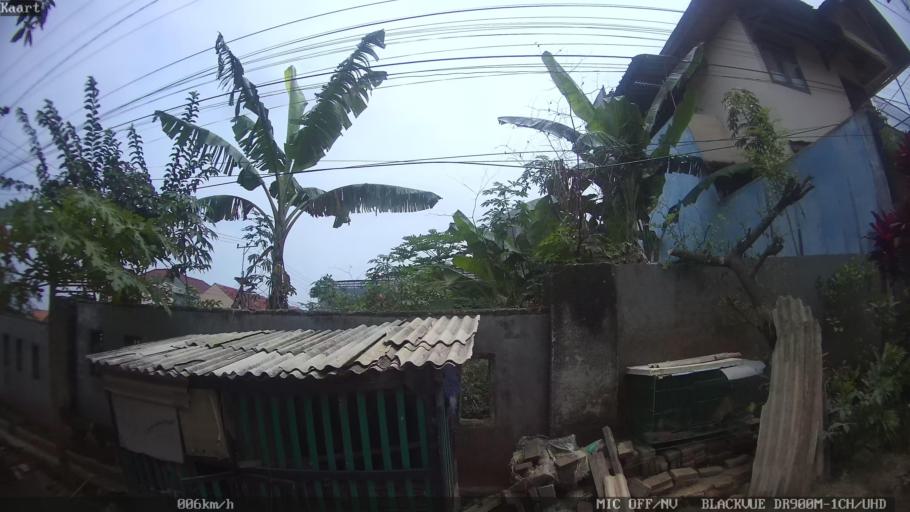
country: ID
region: Lampung
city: Kedaton
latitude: -5.4017
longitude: 105.3242
